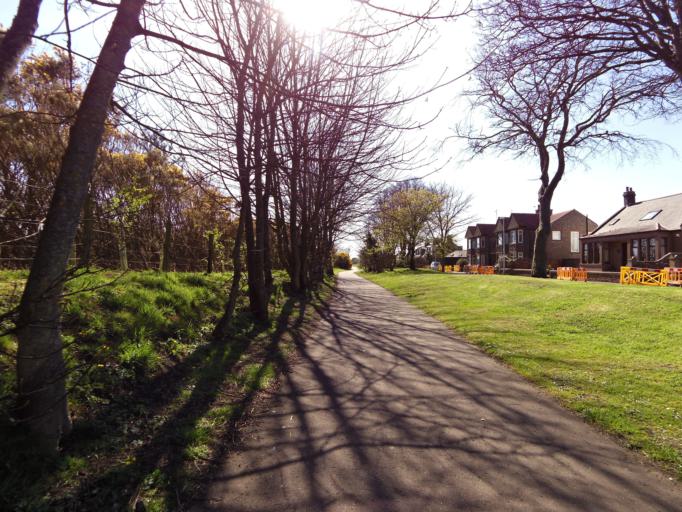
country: GB
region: Scotland
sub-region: Angus
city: Montrose
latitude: 56.7183
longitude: -2.4582
